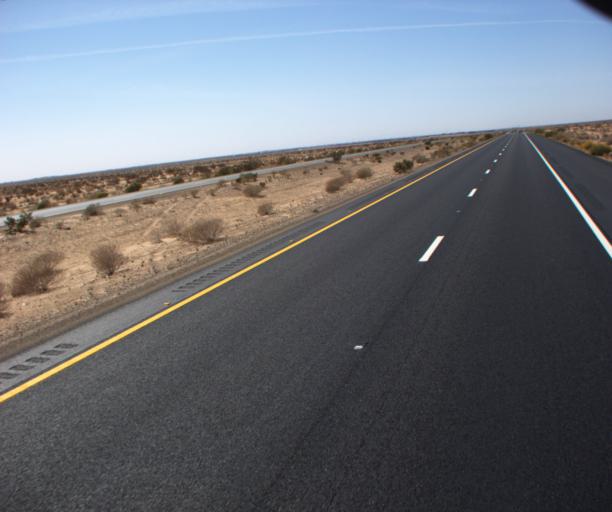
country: US
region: Arizona
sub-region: Yuma County
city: Somerton
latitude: 32.4954
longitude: -114.6062
